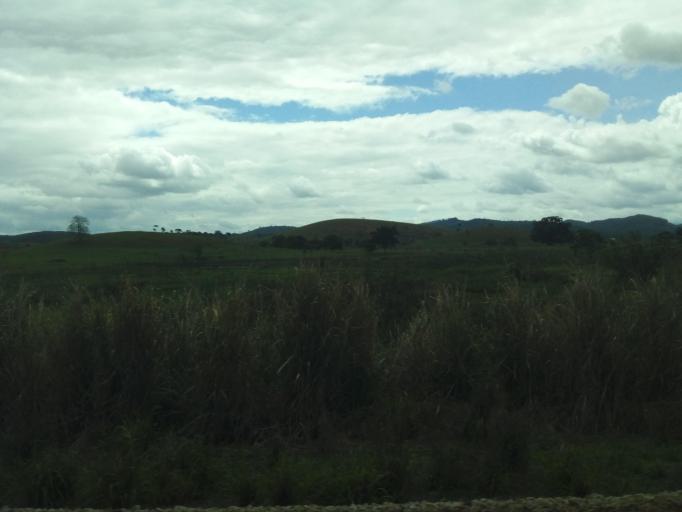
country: BR
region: Minas Gerais
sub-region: Governador Valadares
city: Governador Valadares
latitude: -19.0573
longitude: -42.1468
